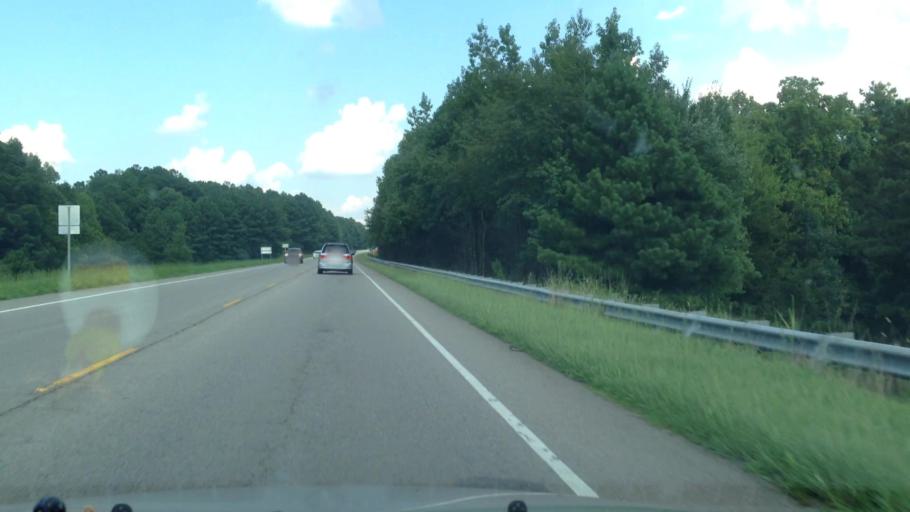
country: US
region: North Carolina
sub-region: Lee County
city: Broadway
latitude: 35.4386
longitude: -79.0523
